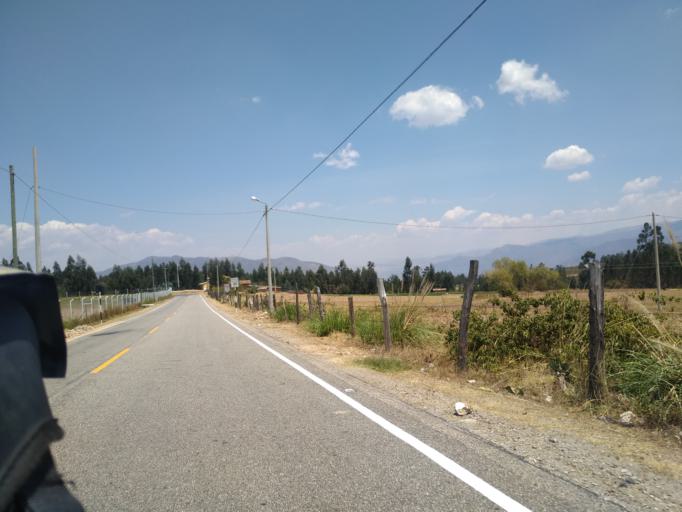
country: PE
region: Cajamarca
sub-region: San Marcos
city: San Marcos
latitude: -7.2893
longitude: -78.2062
